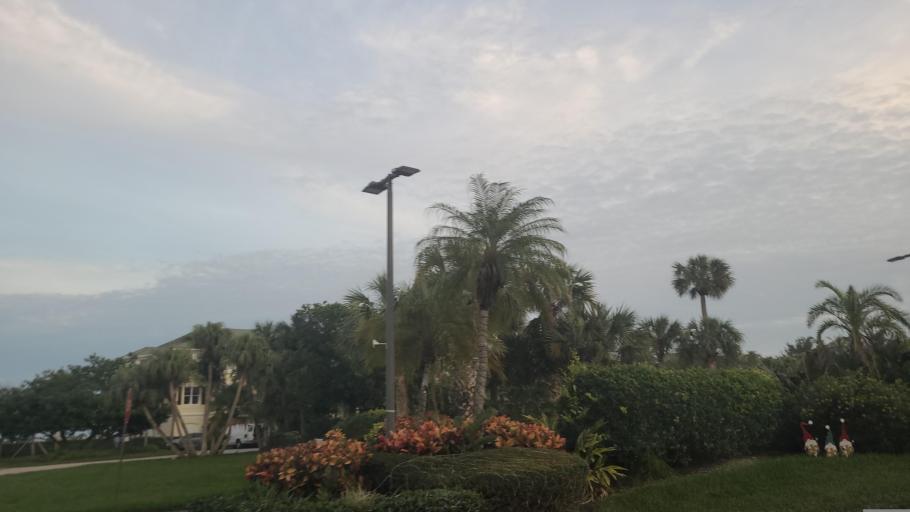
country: US
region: Florida
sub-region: Indian River County
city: Vero Beach
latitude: 27.6379
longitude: -80.3771
